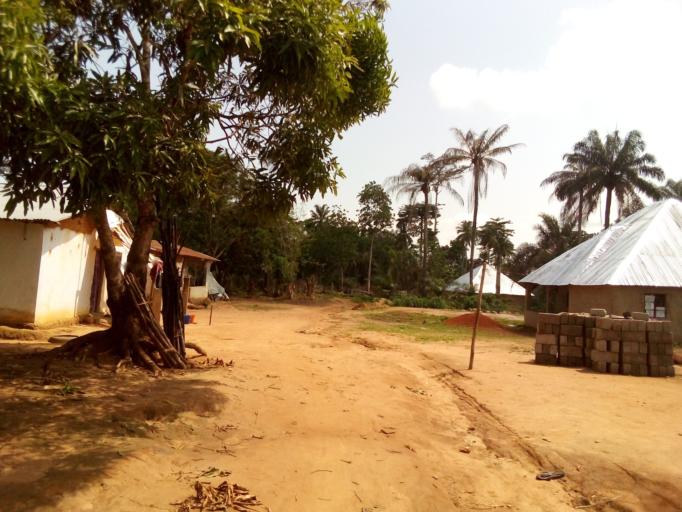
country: SL
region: Western Area
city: Waterloo
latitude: 8.3537
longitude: -13.0184
